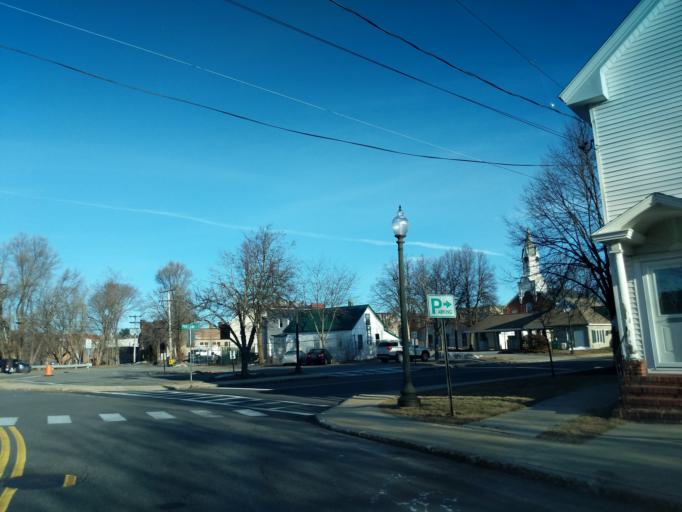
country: US
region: New Hampshire
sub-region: Strafford County
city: Rochester
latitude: 43.3022
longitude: -70.9760
